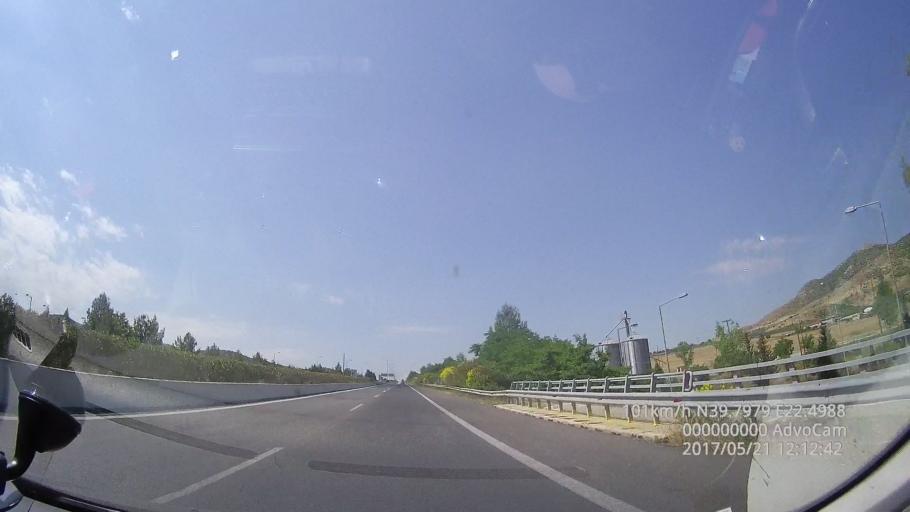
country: GR
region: Thessaly
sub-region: Nomos Larisis
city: Makrychori
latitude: 39.7979
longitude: 22.4988
